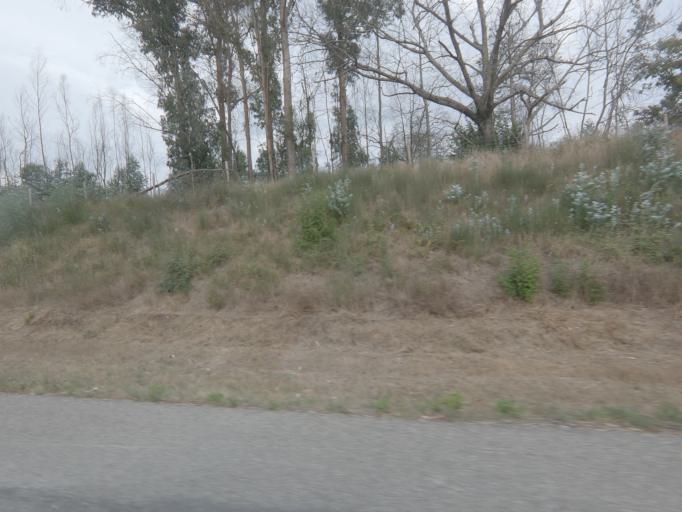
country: PT
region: Viseu
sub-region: Santa Comba Dao
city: Santa Comba Dao
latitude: 40.4207
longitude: -8.1216
